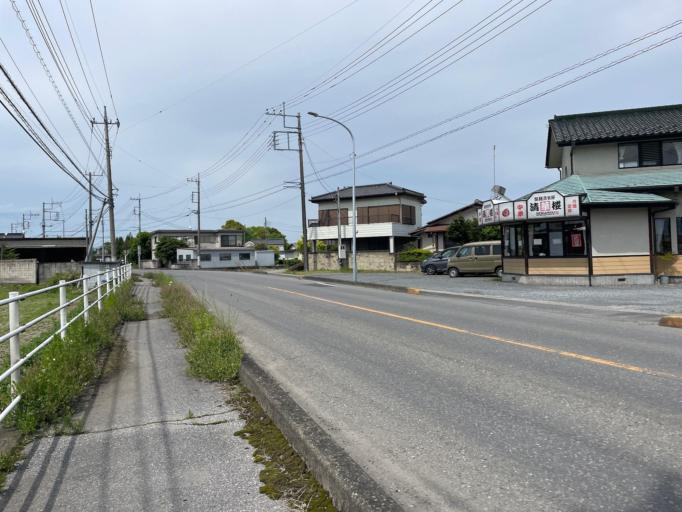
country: JP
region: Tochigi
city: Mibu
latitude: 36.4710
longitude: 139.7648
